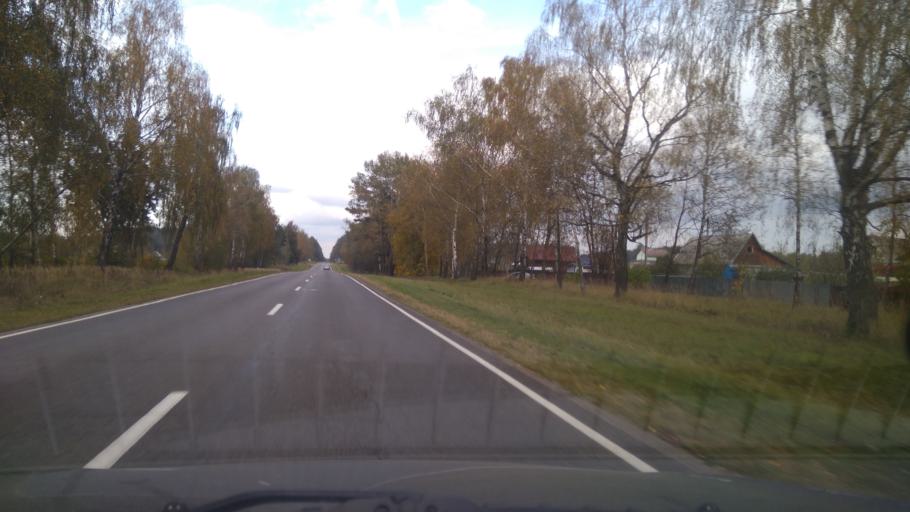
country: BY
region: Minsk
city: Rudzyensk
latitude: 53.6218
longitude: 27.8619
